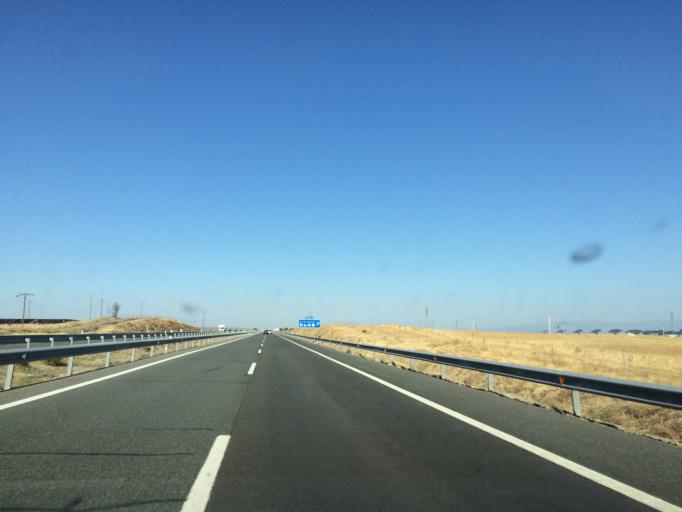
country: ES
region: Castille-La Mancha
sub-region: Province of Toledo
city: Caleruela
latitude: 39.8952
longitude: -5.3189
